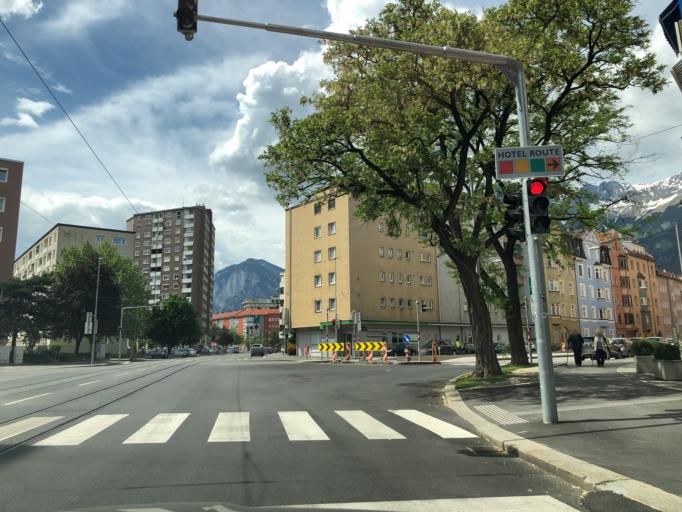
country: AT
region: Tyrol
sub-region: Innsbruck Stadt
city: Innsbruck
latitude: 47.2627
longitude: 11.4116
